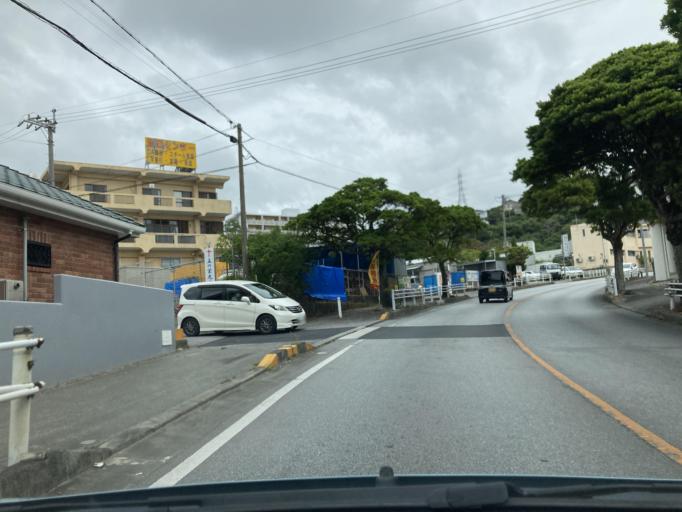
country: JP
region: Okinawa
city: Ginowan
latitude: 26.2350
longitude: 127.7525
